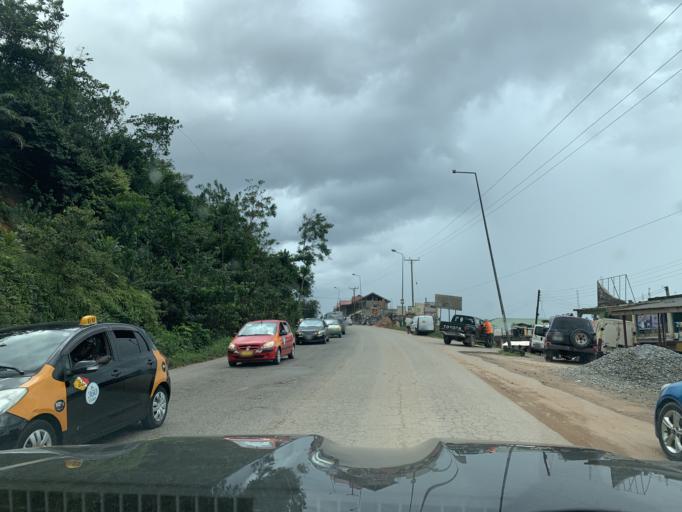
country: GH
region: Western
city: Tarkwa
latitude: 5.3258
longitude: -1.9823
